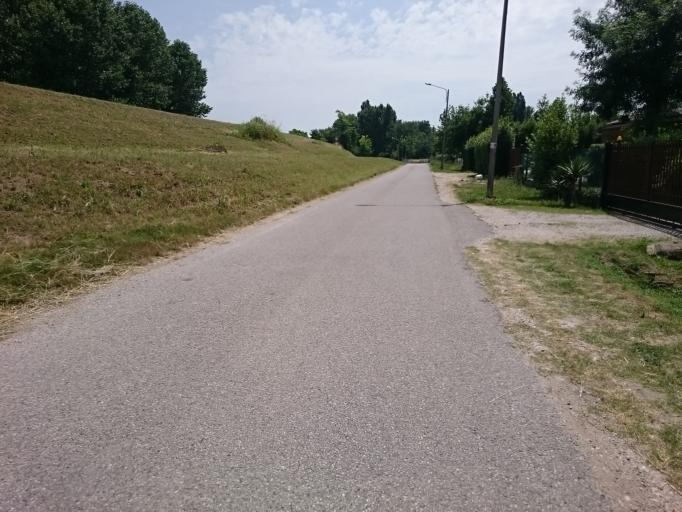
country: IT
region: Veneto
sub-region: Provincia di Padova
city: Codevigo
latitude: 45.2321
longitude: 12.1161
